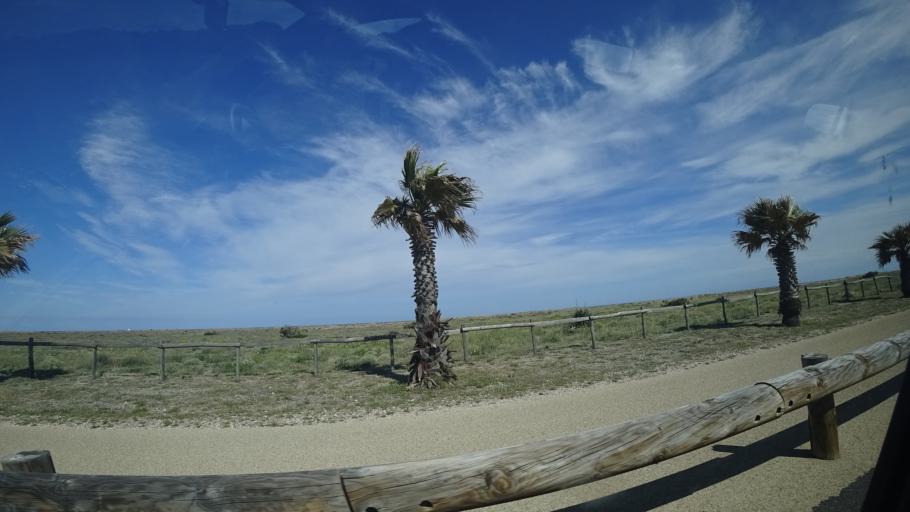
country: FR
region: Languedoc-Roussillon
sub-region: Departement des Pyrenees-Orientales
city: Le Barcares
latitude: 42.8180
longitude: 3.0383
